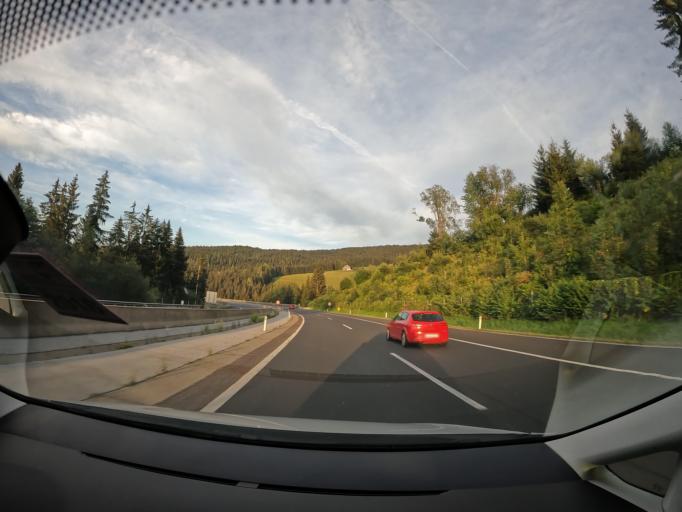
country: AT
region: Styria
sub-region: Politischer Bezirk Voitsberg
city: Voitsberg
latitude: 46.9899
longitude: 15.1327
